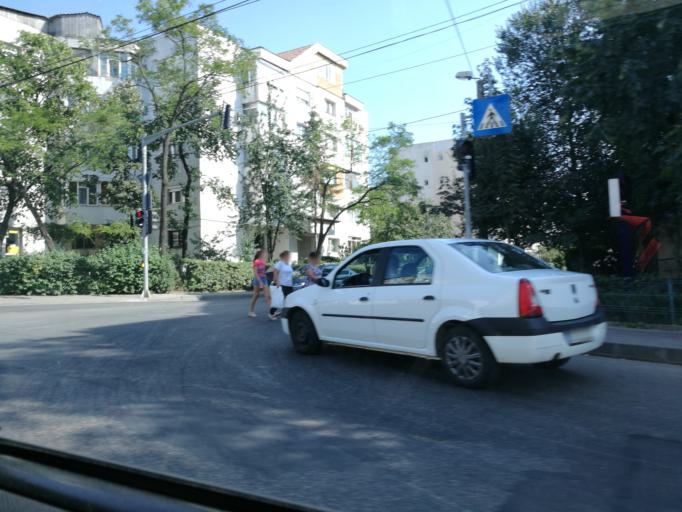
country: RO
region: Iasi
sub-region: Comuna Miroslava
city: Miroslava
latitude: 47.1733
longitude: 27.5460
